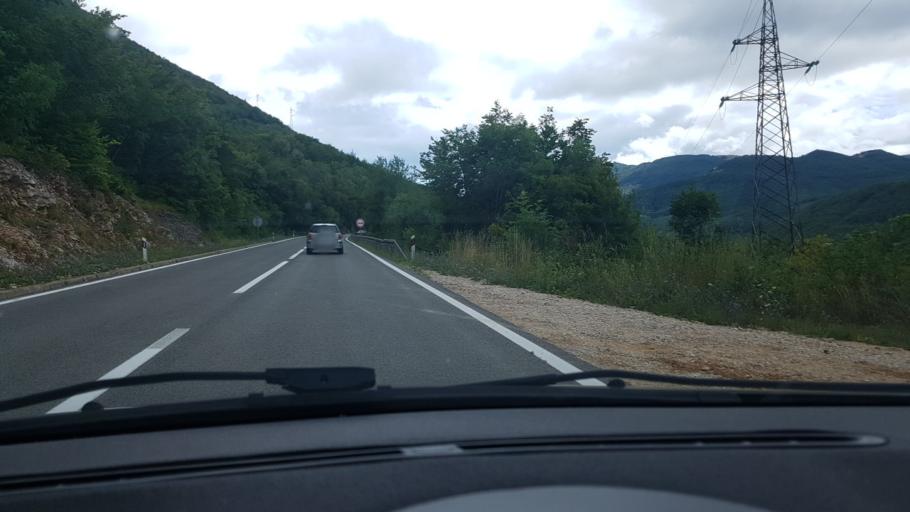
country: HR
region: Zadarska
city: Gracac
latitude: 44.2872
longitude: 15.8282
